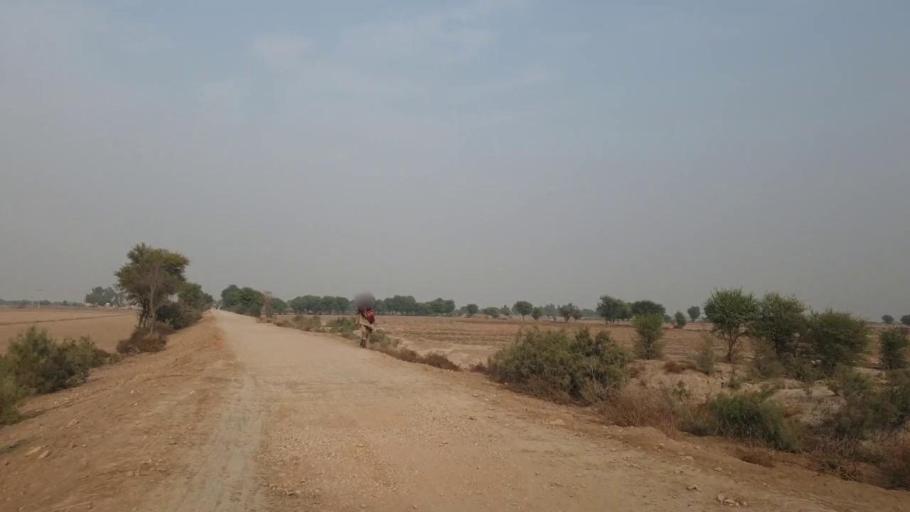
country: PK
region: Sindh
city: Sann
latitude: 26.1036
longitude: 68.0795
